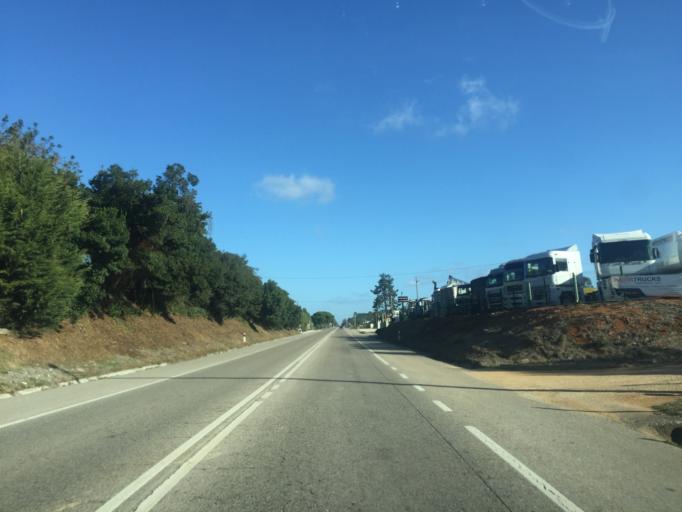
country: PT
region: Leiria
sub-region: Alcobaca
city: Benedita
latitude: 39.4409
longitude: -8.9538
